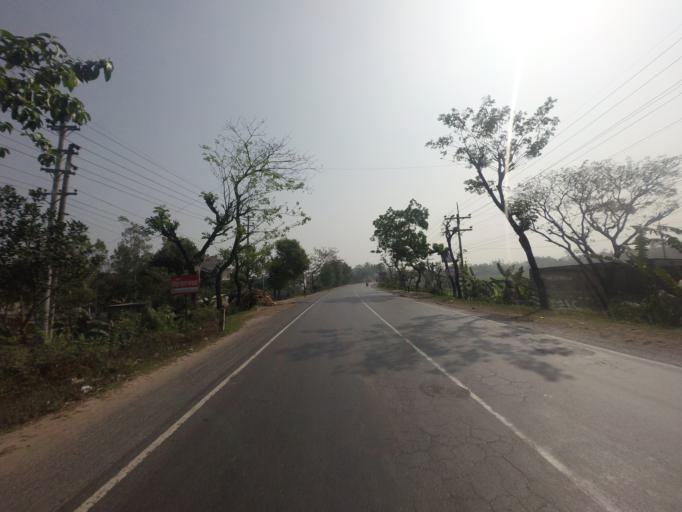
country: BD
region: Dhaka
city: Narsingdi
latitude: 23.8561
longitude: 90.6432
